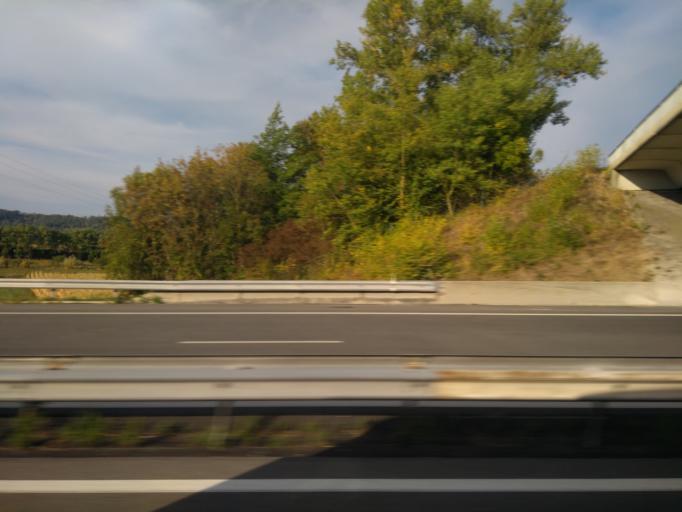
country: FR
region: Rhone-Alpes
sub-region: Departement de l'Isere
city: Cessieu
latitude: 45.5492
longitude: 5.3706
